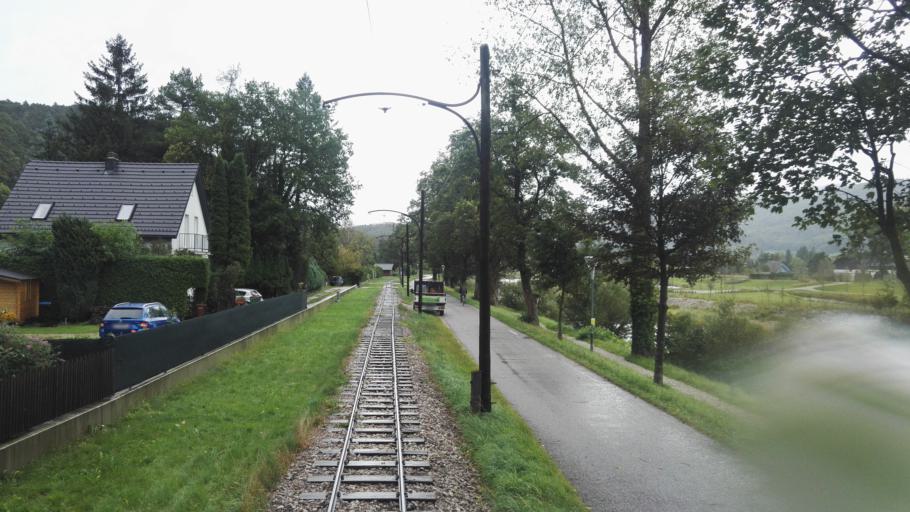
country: AT
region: Lower Austria
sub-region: Politischer Bezirk Neunkirchen
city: Reichenau an der Rax
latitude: 47.7026
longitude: 15.8322
